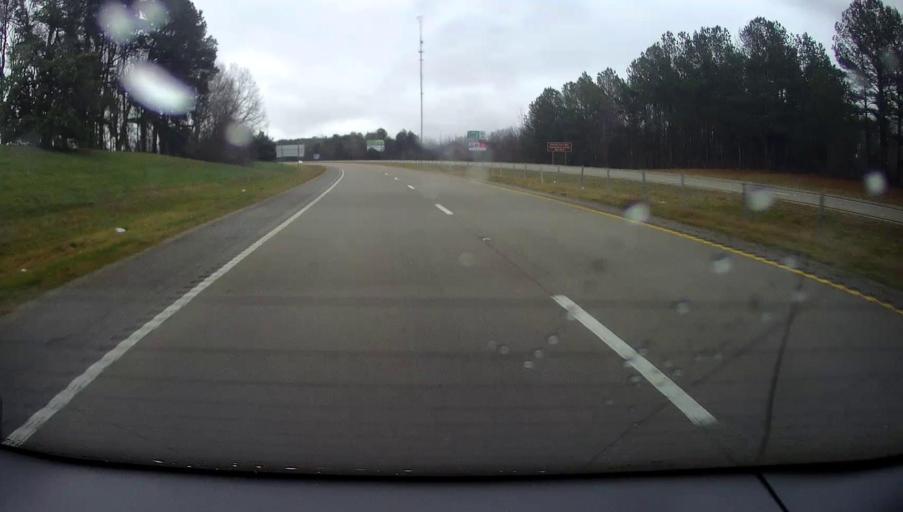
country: US
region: Mississippi
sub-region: Alcorn County
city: Corinth
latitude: 34.9164
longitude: -88.5424
